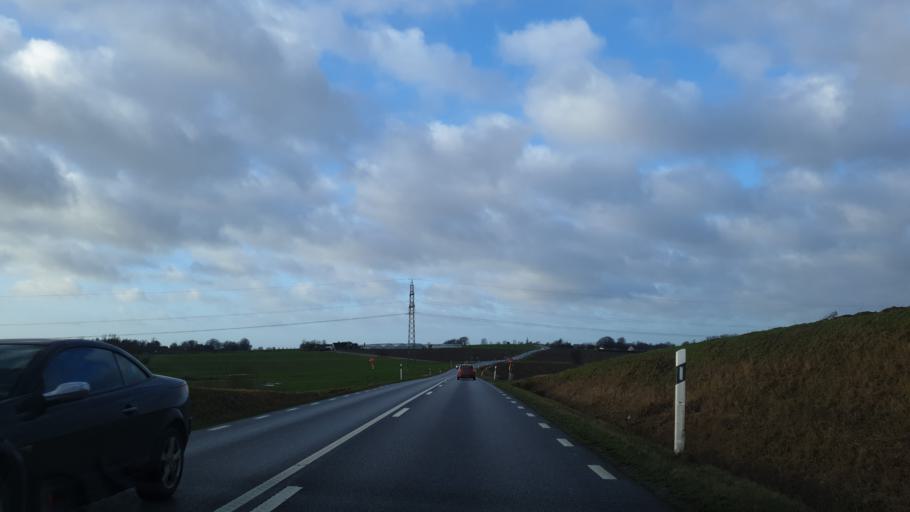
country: SE
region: Skane
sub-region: Svedala Kommun
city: Svedala
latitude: 55.4548
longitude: 13.1754
